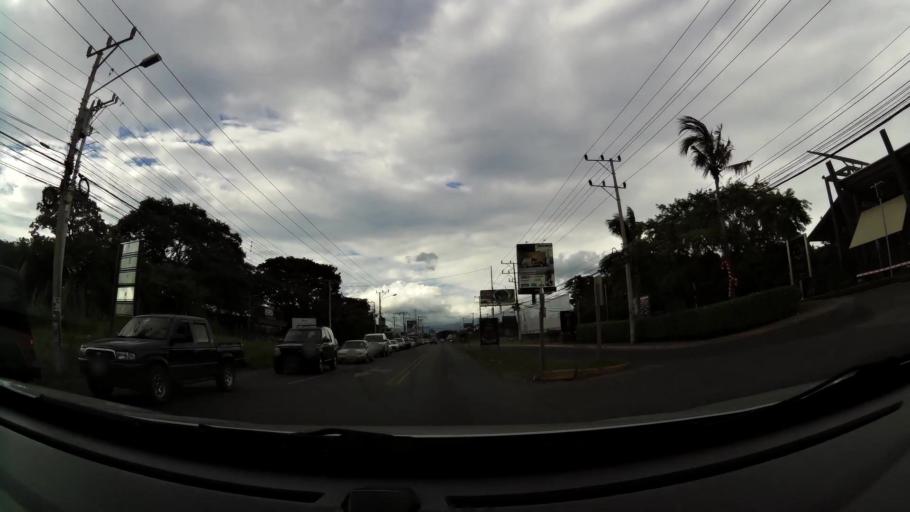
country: CR
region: Heredia
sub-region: Canton de Belen
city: San Antonio
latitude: 9.9596
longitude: -84.1967
